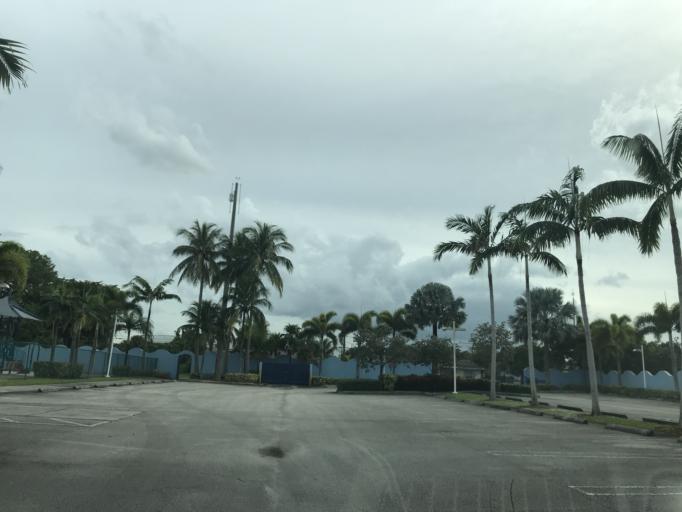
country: US
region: Florida
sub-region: Broward County
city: Margate
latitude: 26.2532
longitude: -80.2094
